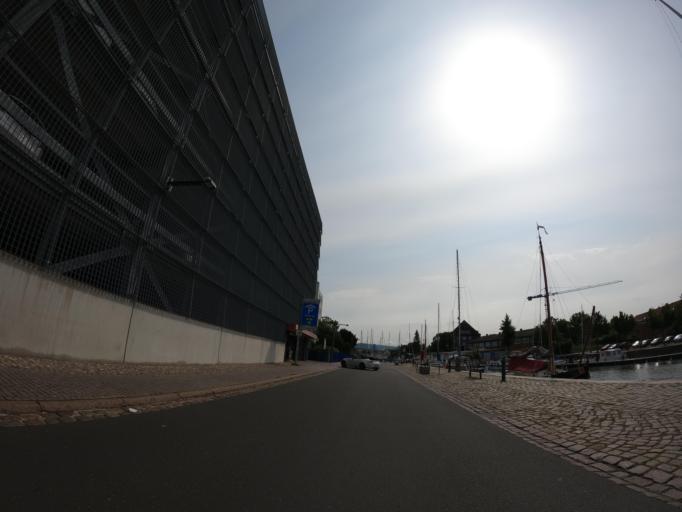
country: DE
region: Mecklenburg-Vorpommern
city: Stralsund
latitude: 54.3133
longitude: 13.0989
